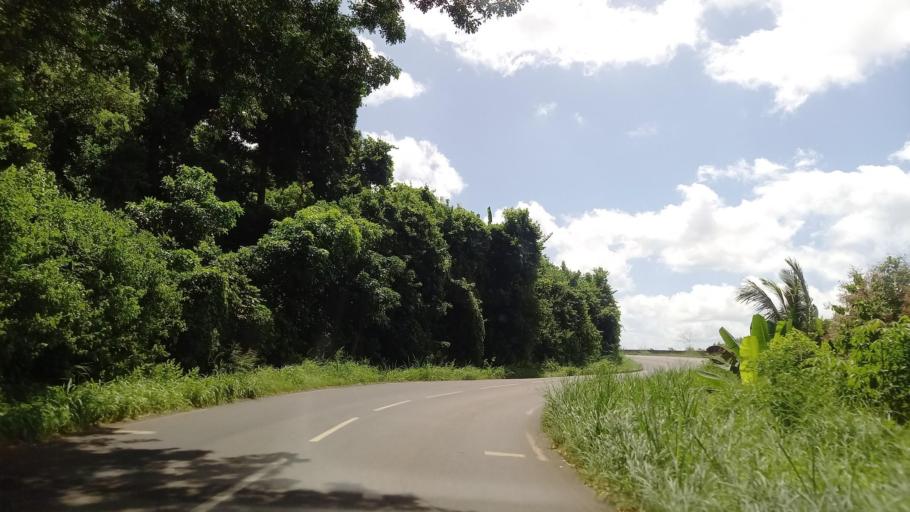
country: YT
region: Bandraboua
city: Bandraboua
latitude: -12.7184
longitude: 45.1295
